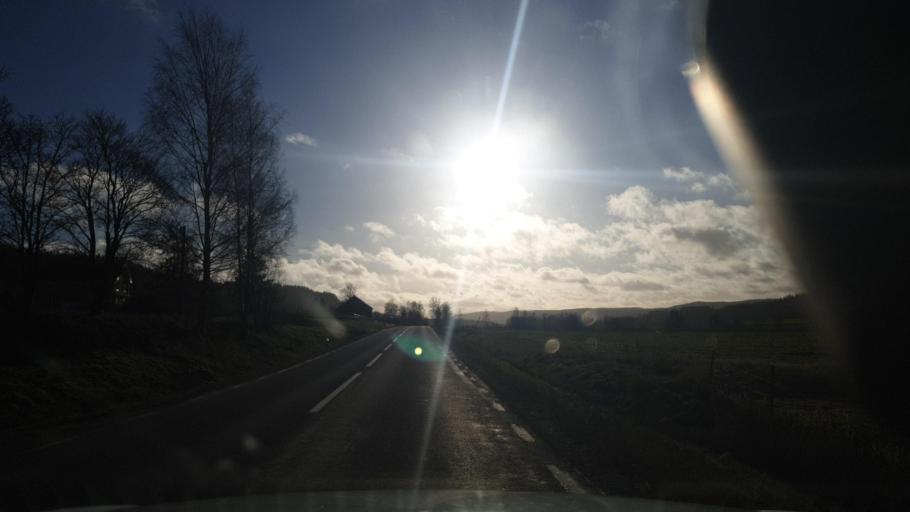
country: SE
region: Vaermland
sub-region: Eda Kommun
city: Amotfors
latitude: 59.6646
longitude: 12.1461
